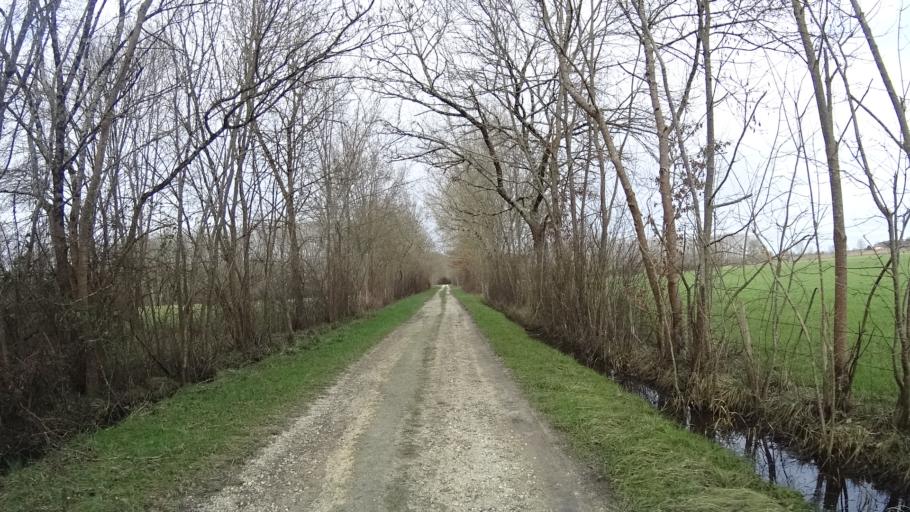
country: FR
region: Aquitaine
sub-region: Departement de la Dordogne
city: Saint-Aulaye
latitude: 45.2121
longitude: 0.1384
